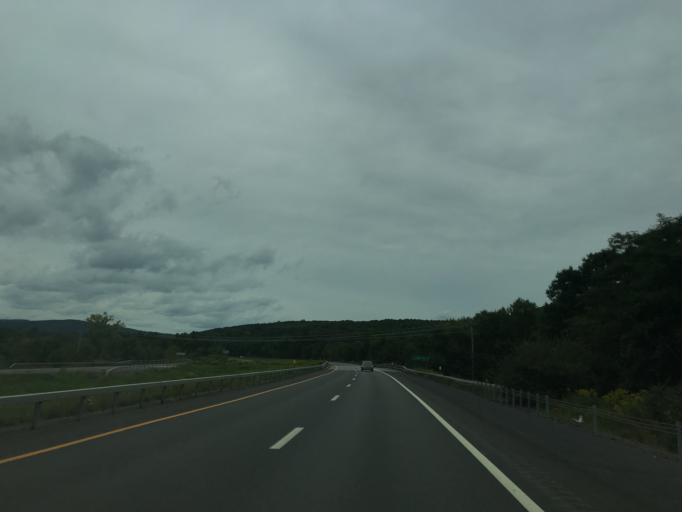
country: US
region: New York
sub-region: Delaware County
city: Sidney
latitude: 42.2939
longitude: -75.3901
